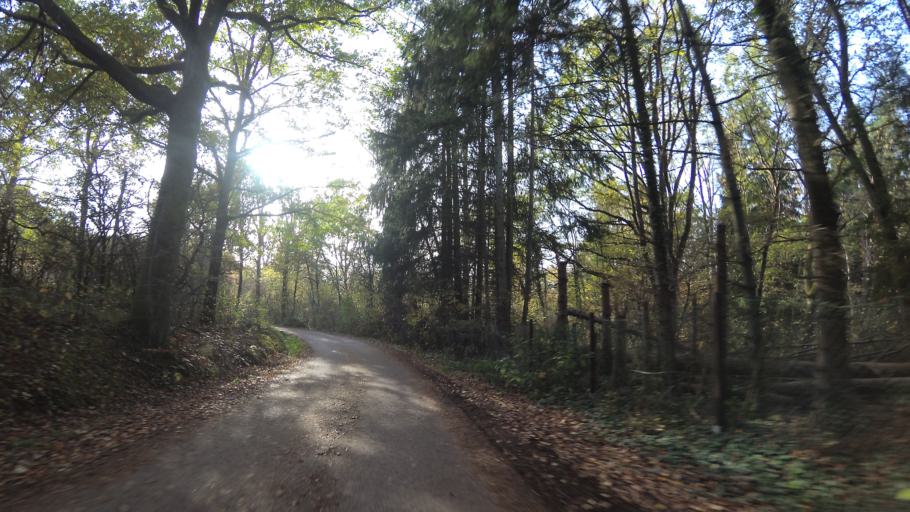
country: DE
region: Saarland
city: Ottweiler
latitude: 49.3851
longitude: 7.1809
